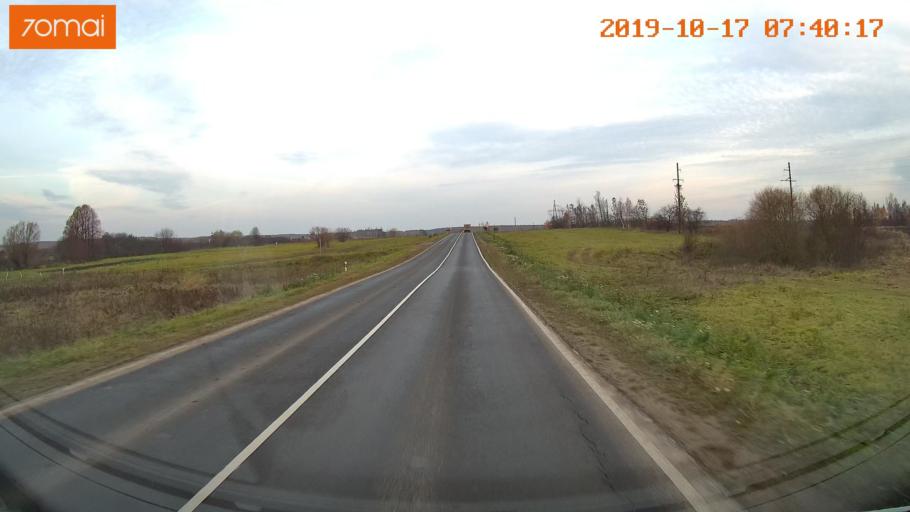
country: RU
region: Vladimir
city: Yur'yev-Pol'skiy
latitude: 56.4712
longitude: 39.8330
